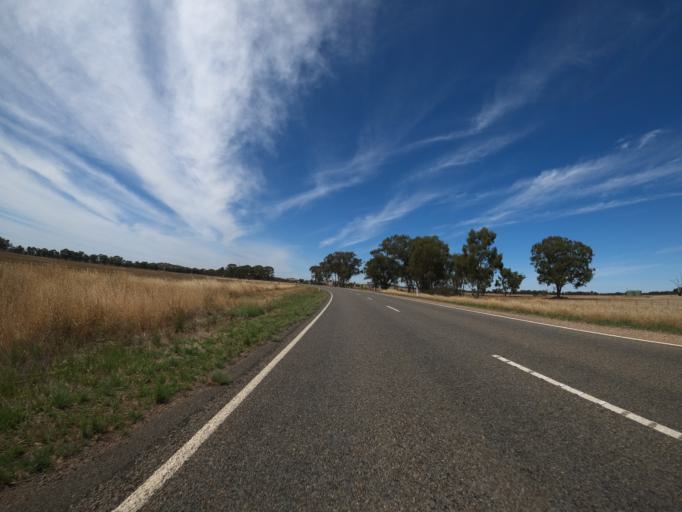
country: AU
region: Victoria
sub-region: Benalla
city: Benalla
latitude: -36.2979
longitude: 145.9524
